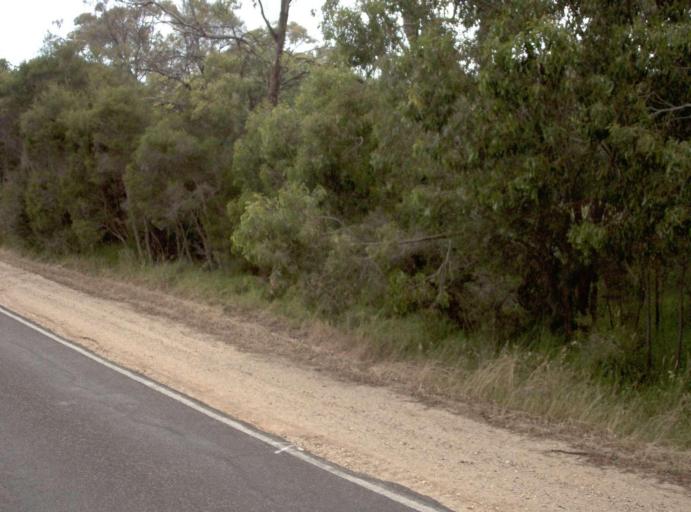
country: AU
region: Victoria
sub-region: Wellington
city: Sale
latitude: -38.1908
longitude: 147.0934
